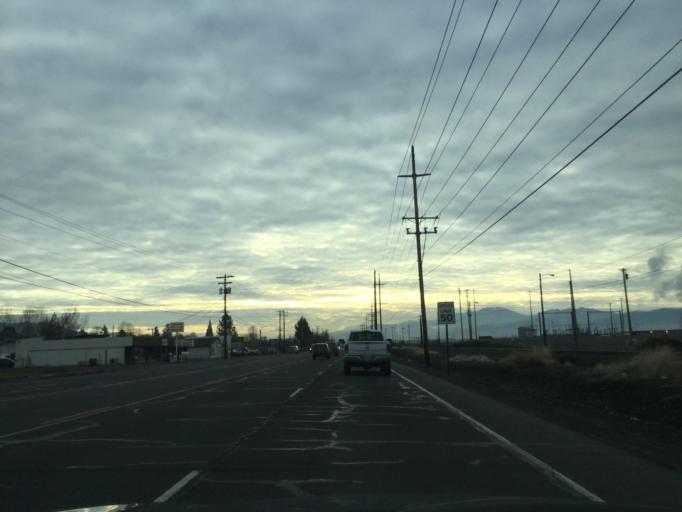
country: US
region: Oregon
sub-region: Jackson County
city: Central Point
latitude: 42.3597
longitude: -122.9053
